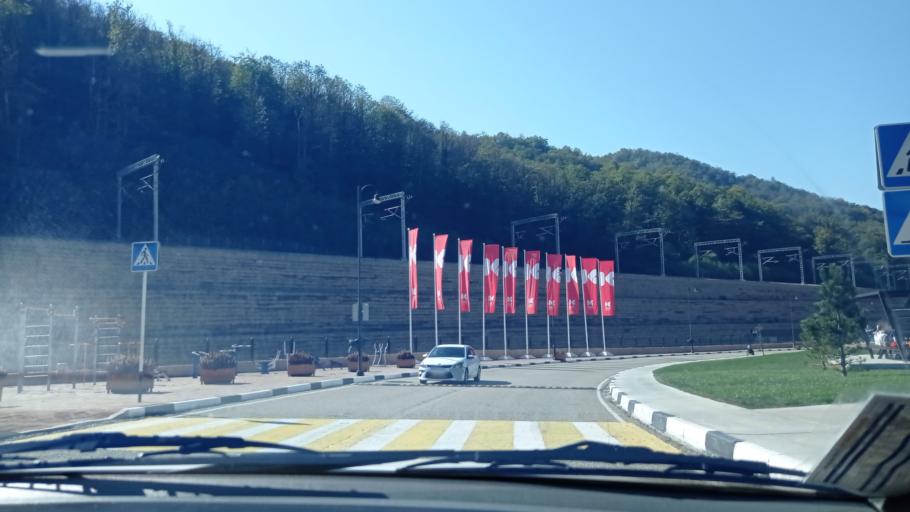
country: RU
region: Krasnodarskiy
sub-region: Sochi City
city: Krasnaya Polyana
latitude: 43.6820
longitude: 40.2640
